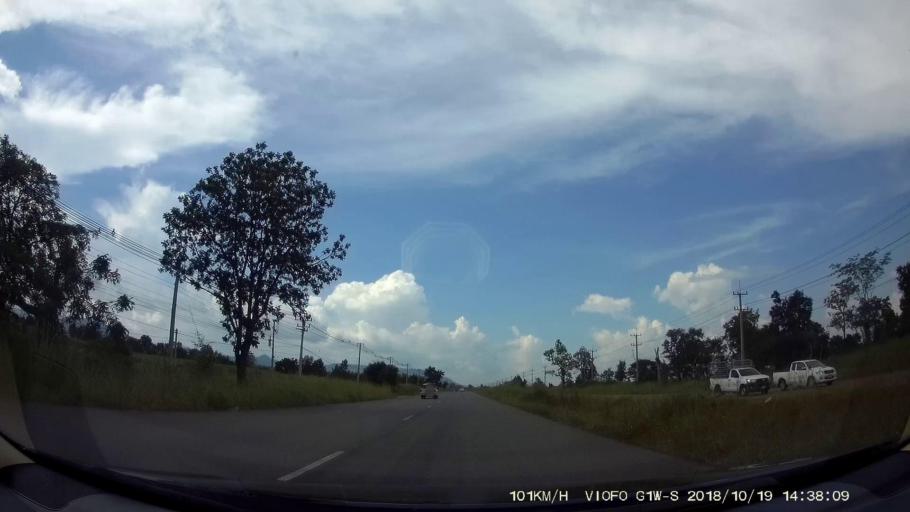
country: TH
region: Chaiyaphum
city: Kaeng Khro
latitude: 16.2074
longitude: 102.2036
